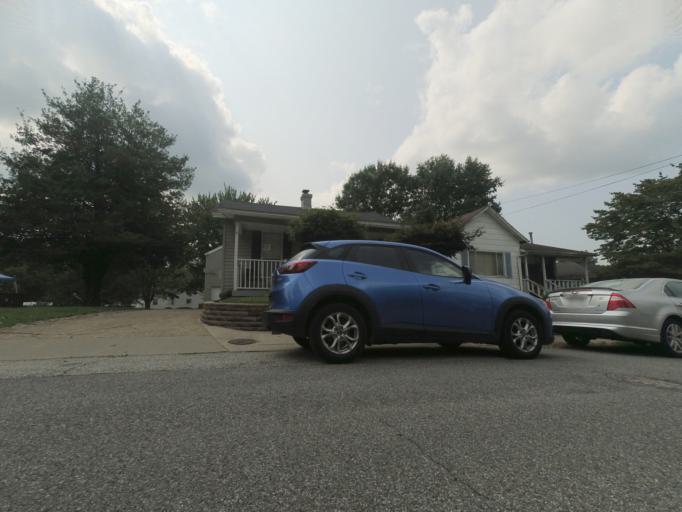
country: US
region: West Virginia
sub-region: Cabell County
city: Huntington
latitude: 38.4023
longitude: -82.4075
